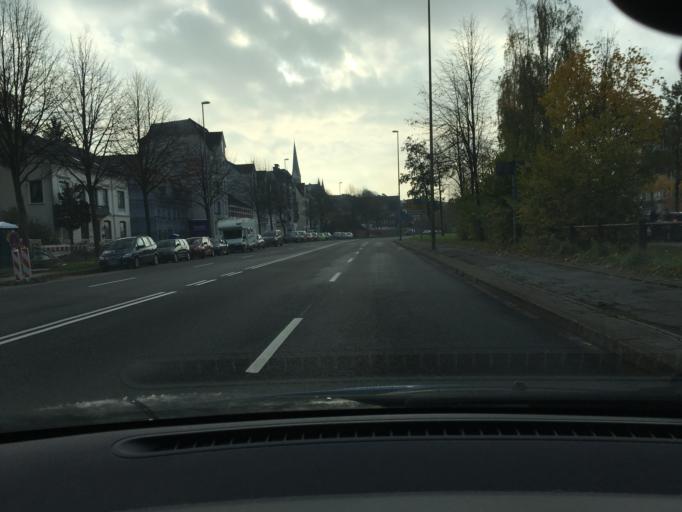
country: DE
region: Schleswig-Holstein
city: Flensburg
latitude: 54.7956
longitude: 9.4385
